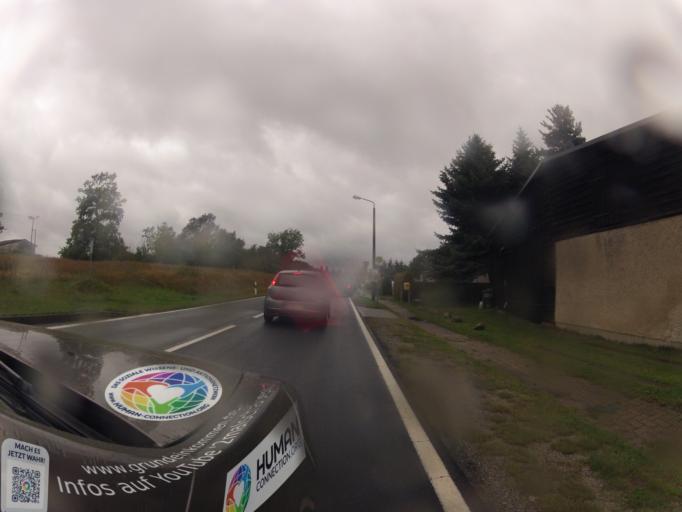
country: DE
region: Mecklenburg-Vorpommern
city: Seebad Bansin
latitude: 53.8869
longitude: 14.0931
